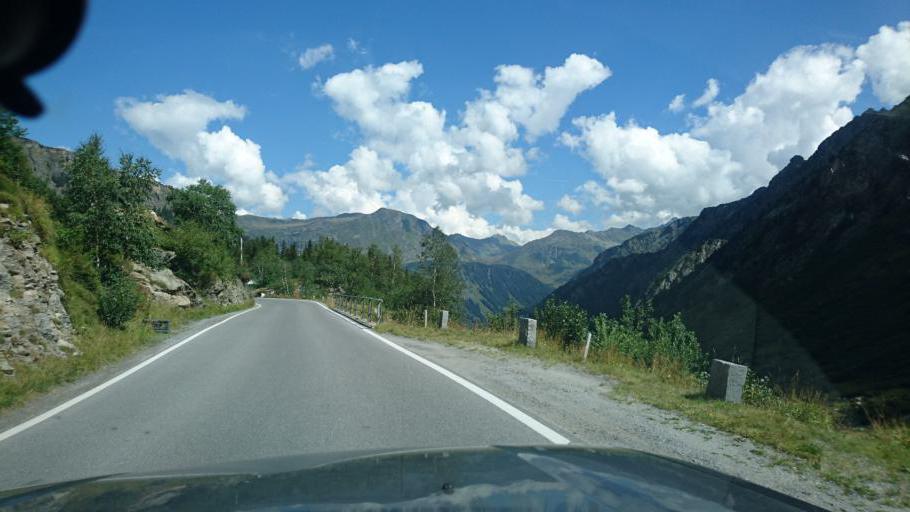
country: AT
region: Vorarlberg
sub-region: Politischer Bezirk Bludenz
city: Gaschurn
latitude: 46.9362
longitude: 10.0607
